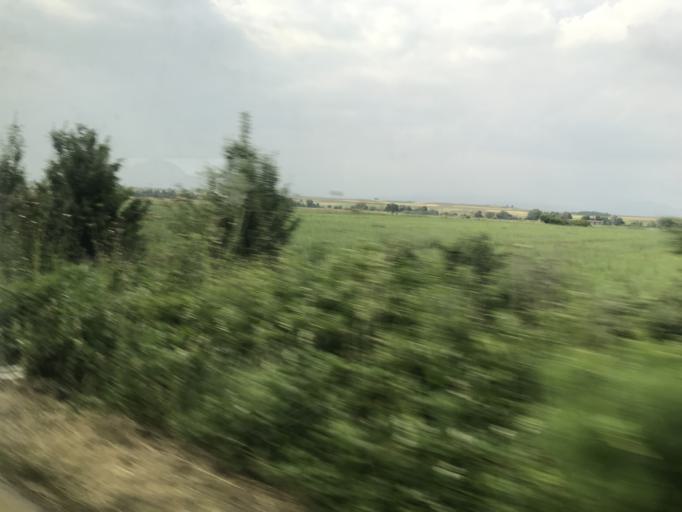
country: GR
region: East Macedonia and Thrace
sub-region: Nomos Rodopis
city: Lykeio
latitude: 41.0419
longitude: 25.6546
